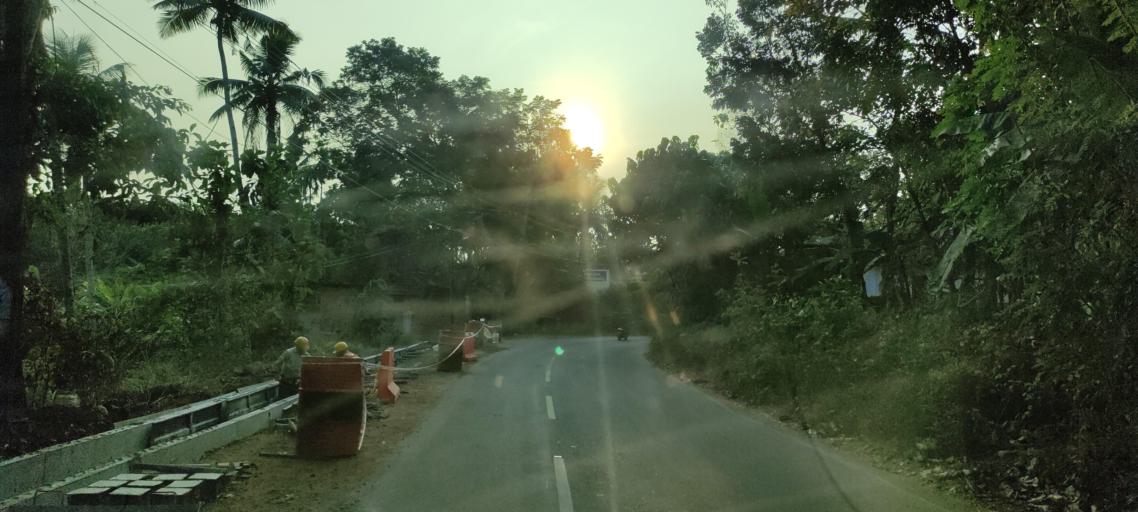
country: IN
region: Kerala
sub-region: Alappuzha
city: Mavelikara
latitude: 9.2500
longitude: 76.5729
